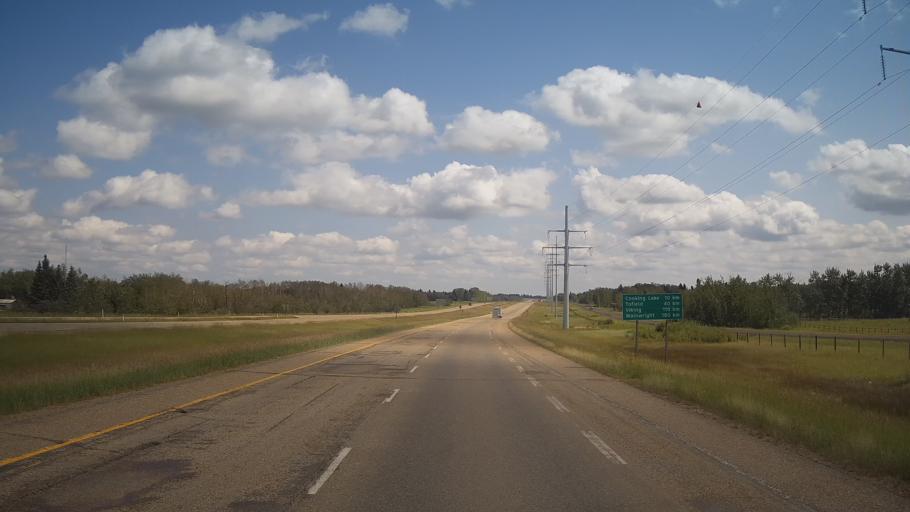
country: CA
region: Alberta
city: Sherwood Park
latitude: 53.4458
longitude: -113.2379
